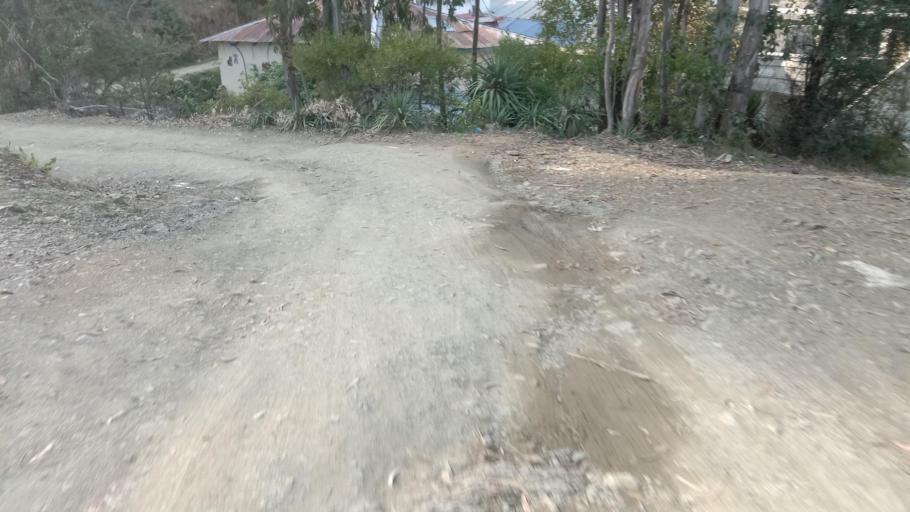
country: PK
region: Khyber Pakhtunkhwa
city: Abbottabad
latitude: 34.2043
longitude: 73.2071
